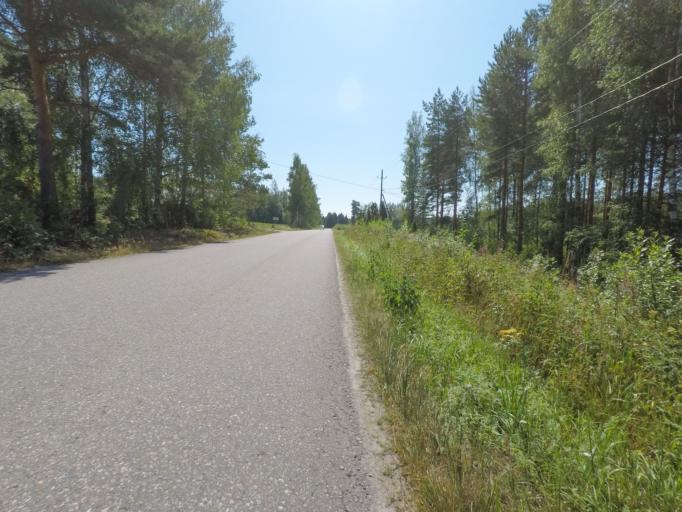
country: FI
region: Southern Savonia
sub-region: Mikkeli
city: Puumala
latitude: 61.4485
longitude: 28.1591
